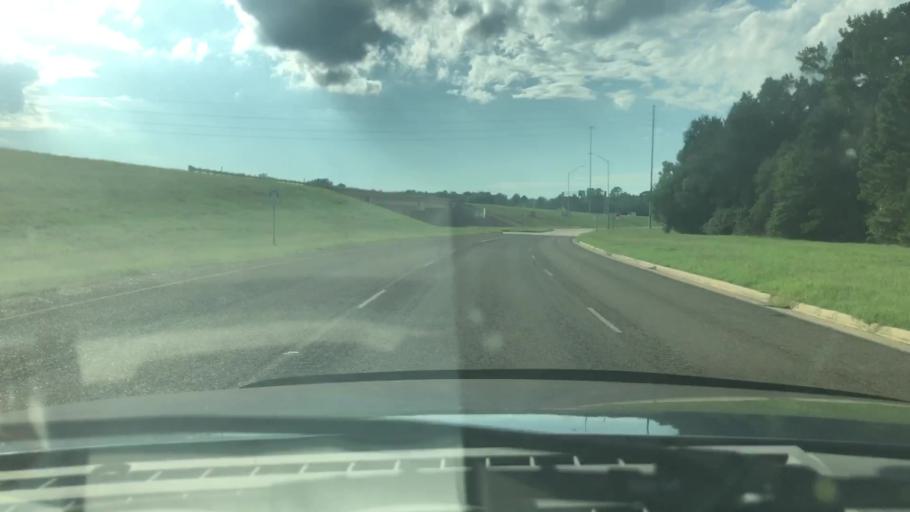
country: US
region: Texas
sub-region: Bowie County
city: Wake Village
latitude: 33.3866
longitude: -94.0901
